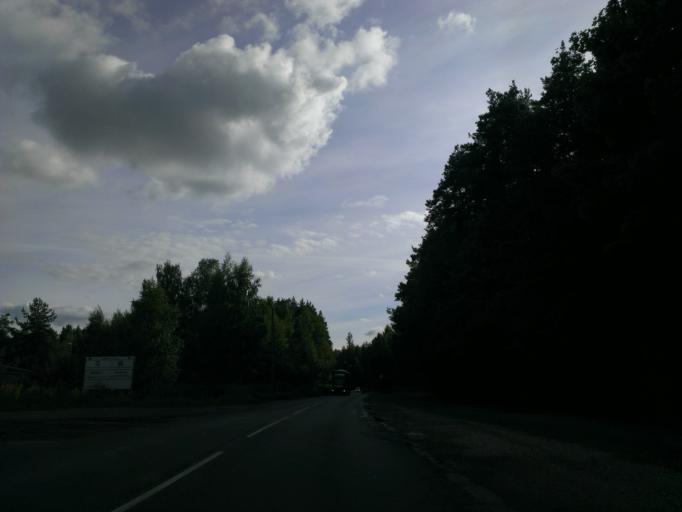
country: LV
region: Stopini
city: Ulbroka
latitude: 56.9703
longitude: 24.2537
